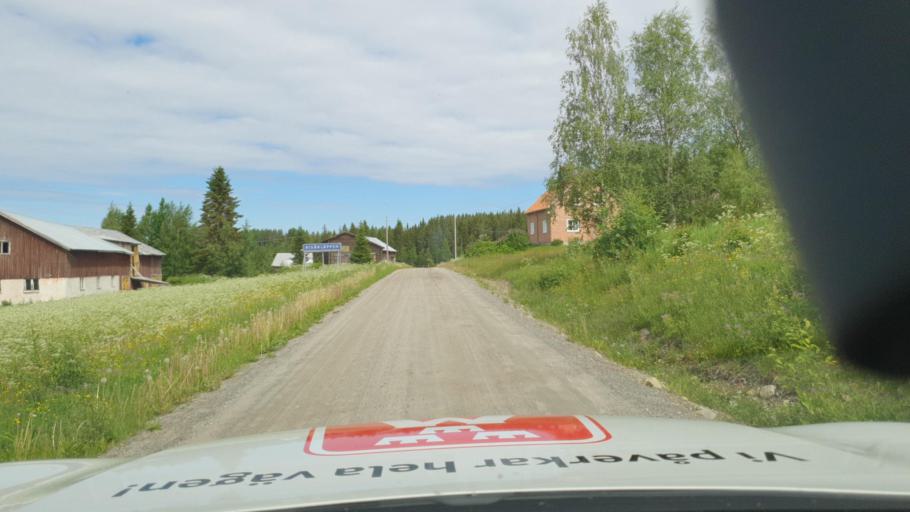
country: SE
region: Vaesterbotten
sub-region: Skelleftea Kommun
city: Langsele
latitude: 64.5929
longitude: 20.2946
